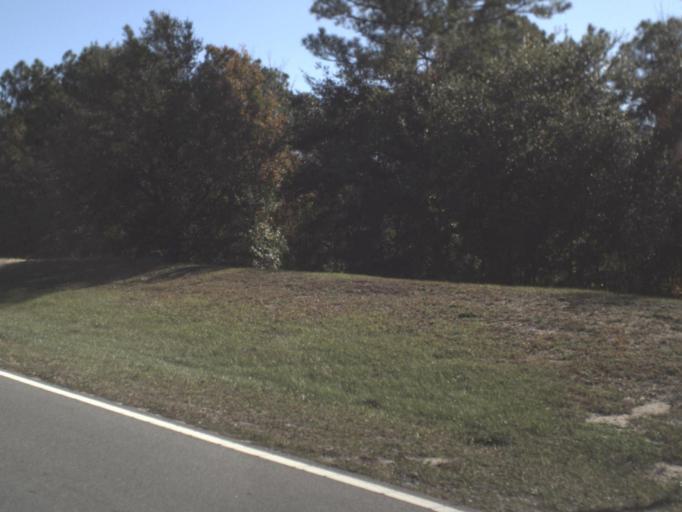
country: US
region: Florida
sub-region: Flagler County
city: Palm Coast
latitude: 29.5528
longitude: -81.2639
